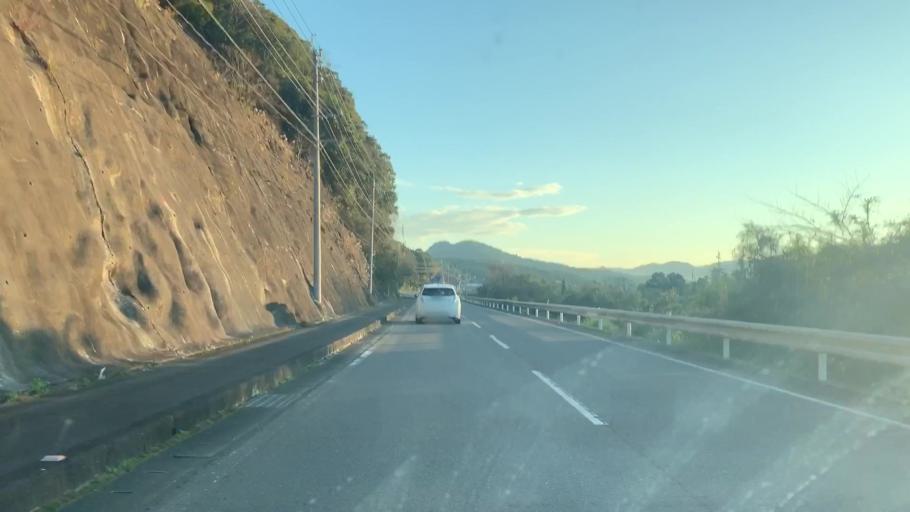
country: JP
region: Saga Prefecture
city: Imaricho-ko
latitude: 33.2734
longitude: 129.9648
